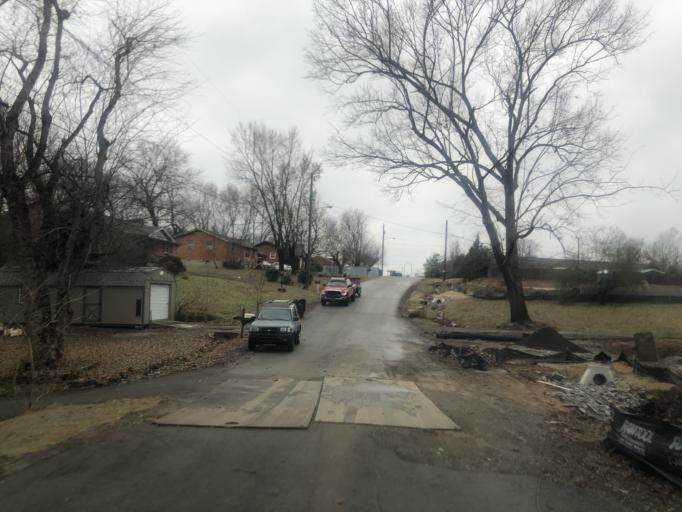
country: US
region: Tennessee
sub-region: Davidson County
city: Lakewood
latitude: 36.1432
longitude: -86.6703
